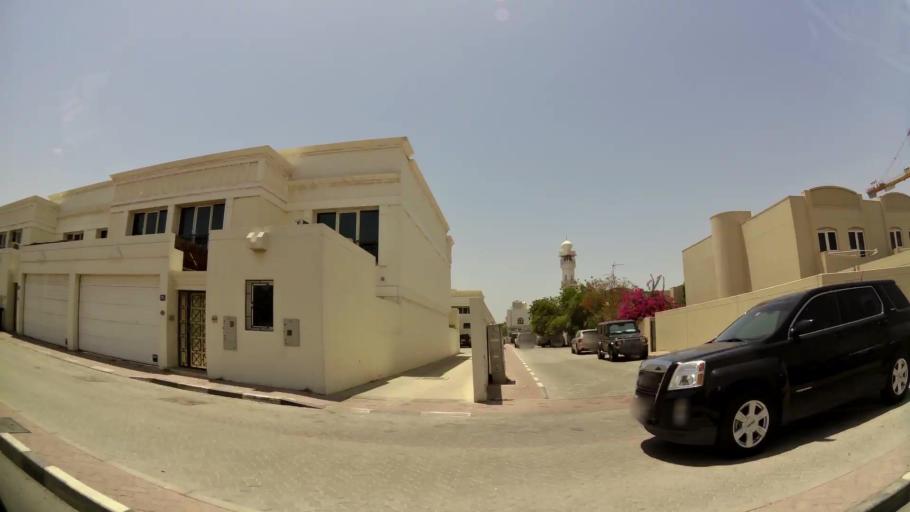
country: AE
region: Dubai
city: Dubai
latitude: 25.2231
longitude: 55.2644
